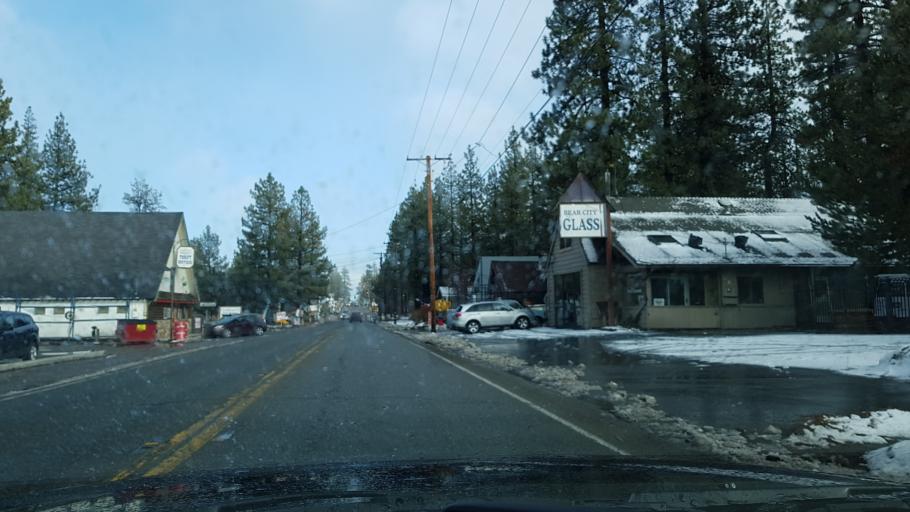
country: US
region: California
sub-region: San Bernardino County
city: Big Bear City
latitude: 34.2611
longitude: -116.8489
